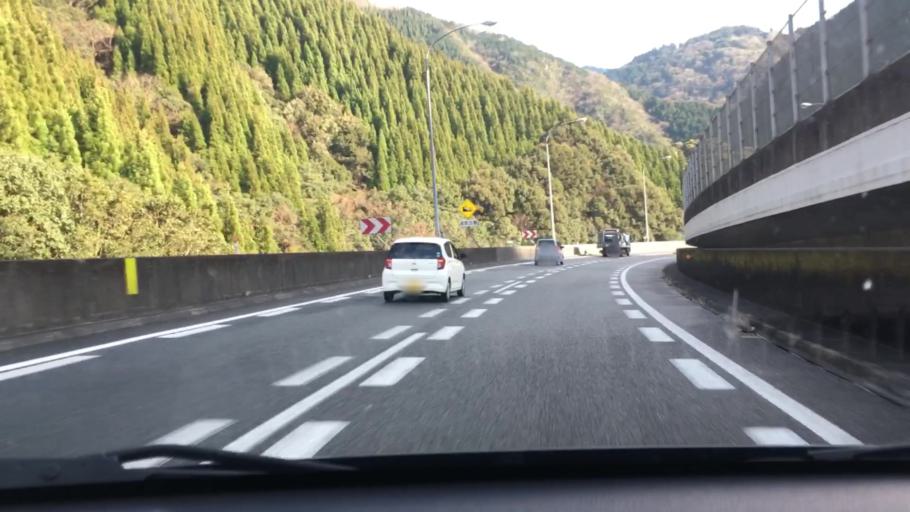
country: JP
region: Kumamoto
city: Hitoyoshi
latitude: 32.3265
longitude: 130.7566
